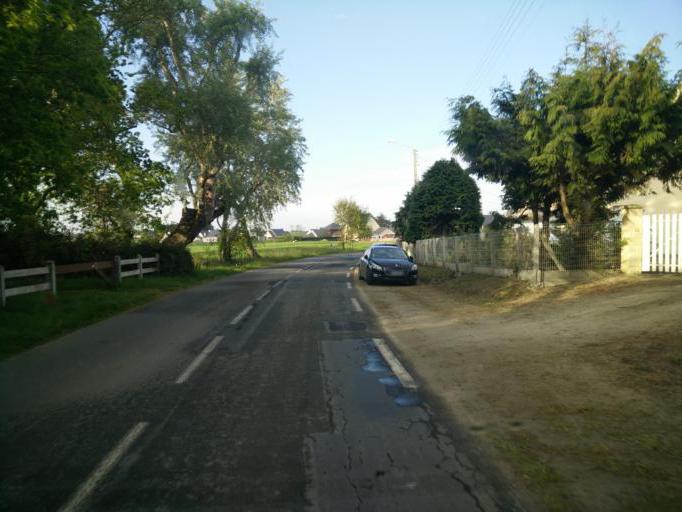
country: FR
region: Brittany
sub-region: Departement des Cotes-d'Armor
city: Plurien
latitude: 48.6475
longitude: -2.3608
